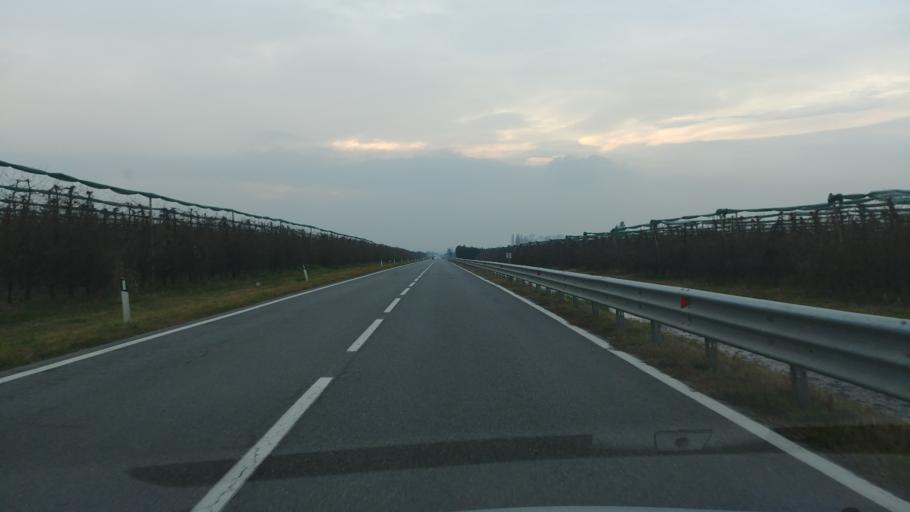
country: IT
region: Piedmont
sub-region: Provincia di Cuneo
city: Castelletto Stura
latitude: 44.4439
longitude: 7.6074
